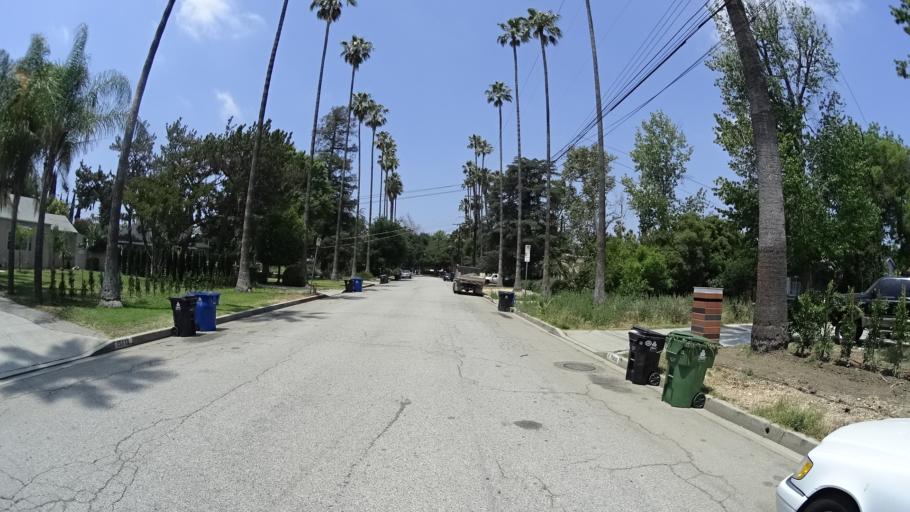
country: US
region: California
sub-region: Los Angeles County
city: Van Nuys
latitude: 34.1887
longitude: -118.4606
